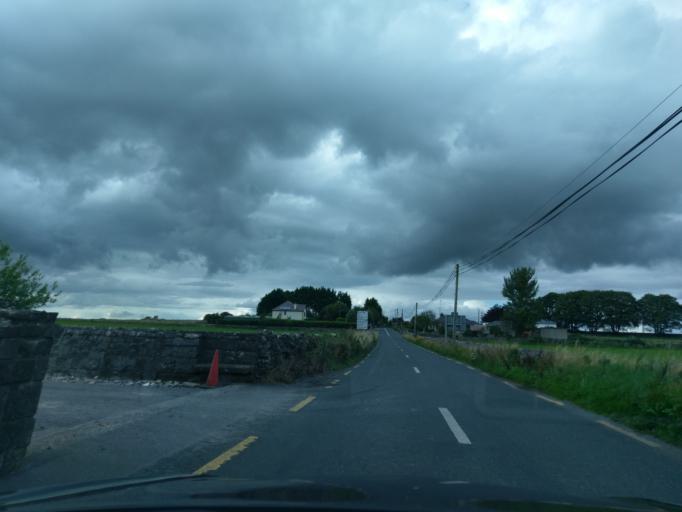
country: IE
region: Connaught
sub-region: County Galway
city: Athenry
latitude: 53.2861
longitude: -8.7443
